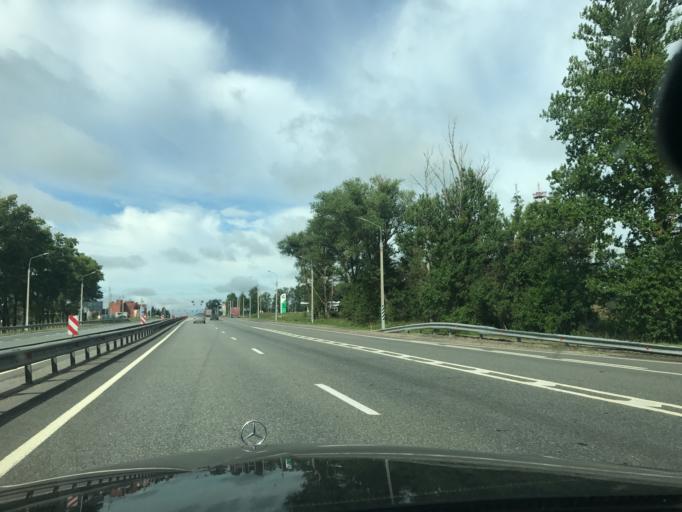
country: RU
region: Smolensk
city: Yartsevo
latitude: 55.0682
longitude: 32.6298
